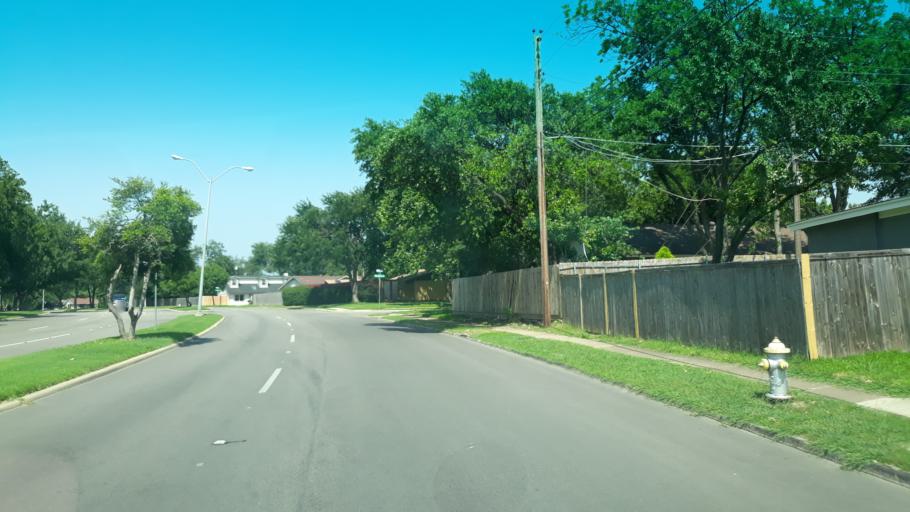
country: US
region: Texas
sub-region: Dallas County
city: Irving
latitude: 32.8562
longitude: -96.9642
